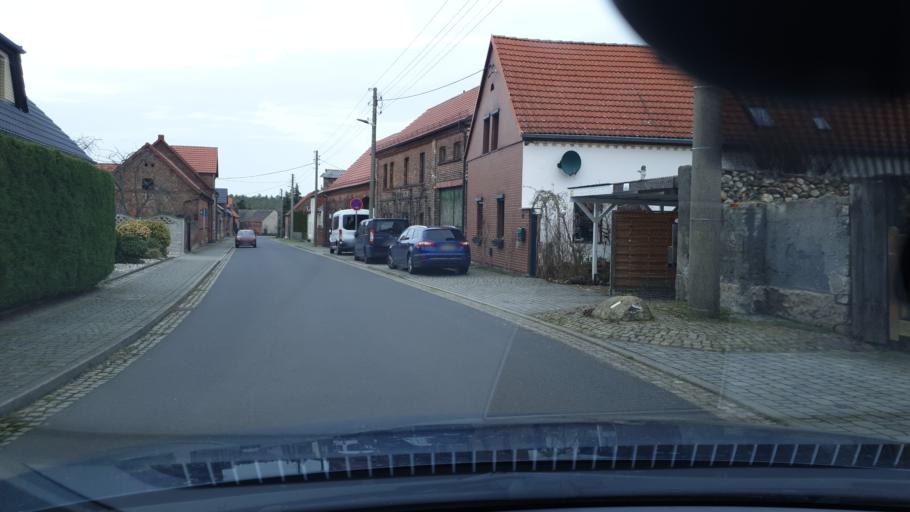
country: DE
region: Saxony-Anhalt
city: Radis
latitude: 51.7630
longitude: 12.5567
